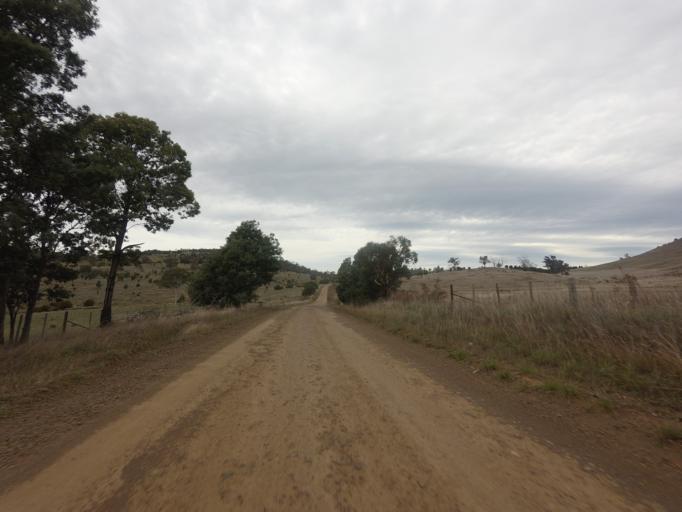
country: AU
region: Tasmania
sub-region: Derwent Valley
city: New Norfolk
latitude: -42.5561
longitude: 146.9146
